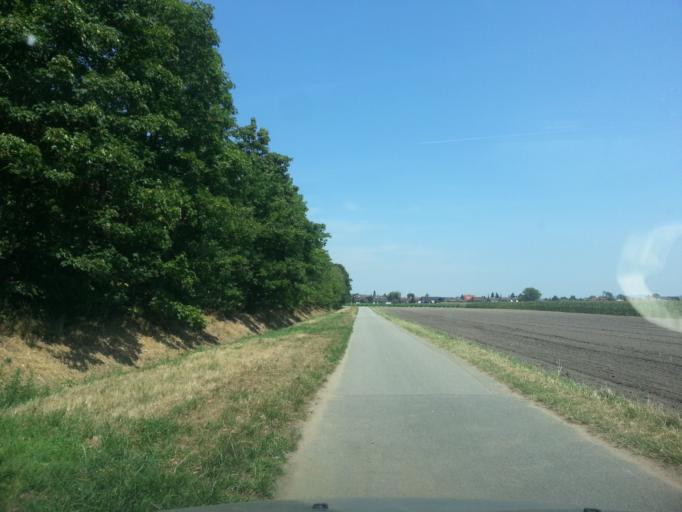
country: DE
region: Hesse
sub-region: Regierungsbezirk Darmstadt
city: Einhausen
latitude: 49.6618
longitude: 8.5467
